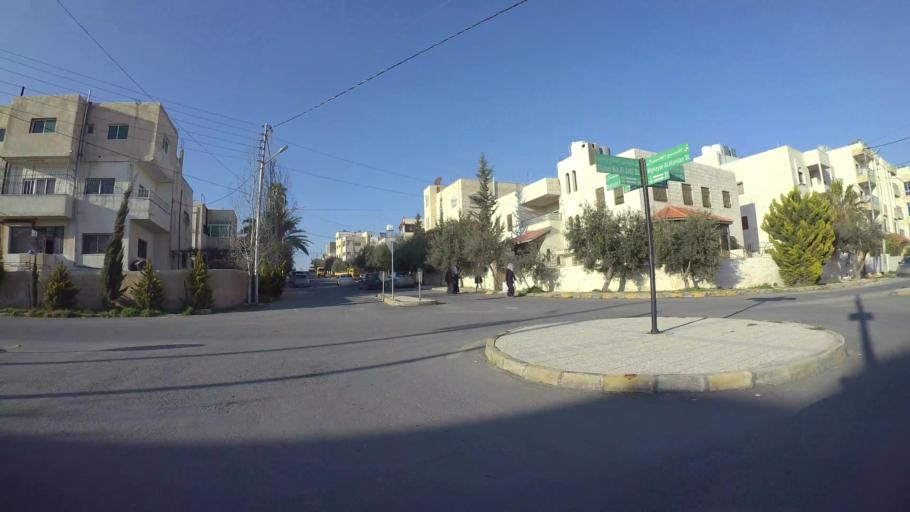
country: JO
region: Amman
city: Al Bunayyat ash Shamaliyah
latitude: 31.8973
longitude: 35.9091
